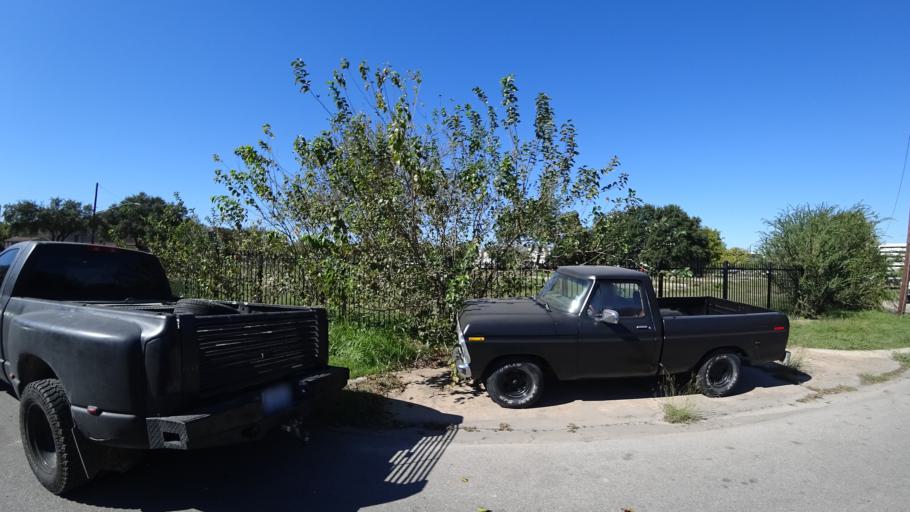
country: US
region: Texas
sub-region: Travis County
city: Austin
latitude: 30.2387
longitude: -97.7227
